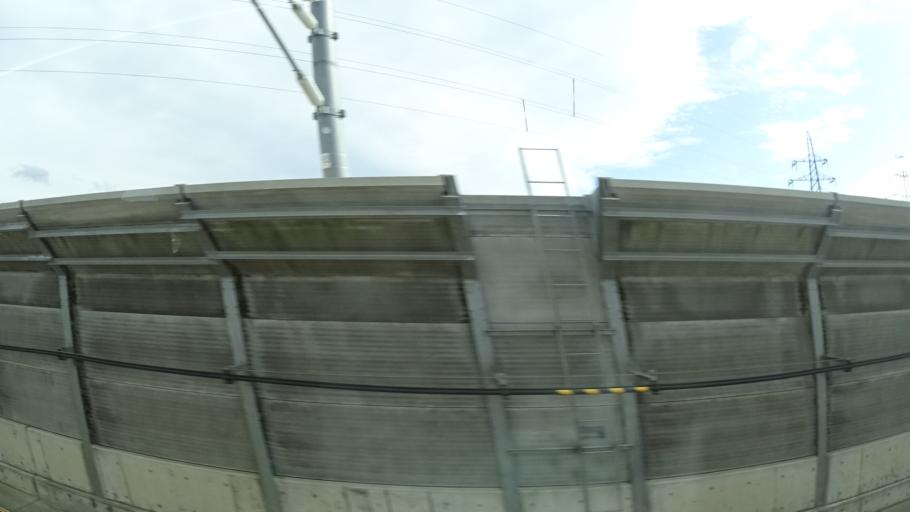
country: JP
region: Toyama
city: Kuragaki-kosugi
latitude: 36.7242
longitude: 137.1367
